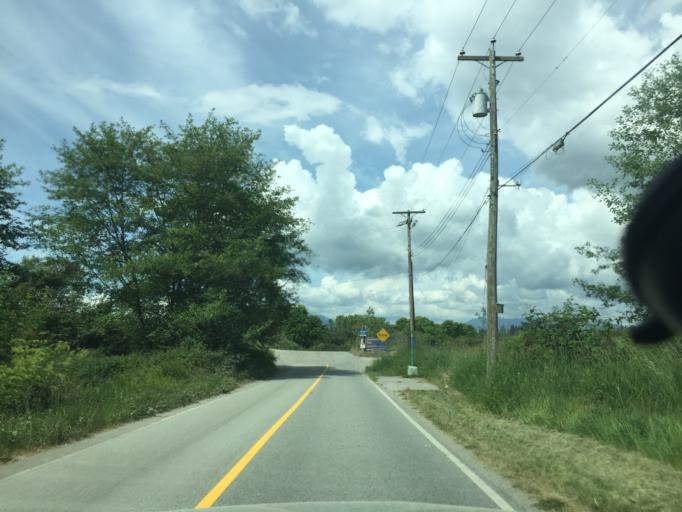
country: CA
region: British Columbia
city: Richmond
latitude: 49.2116
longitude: -123.1698
